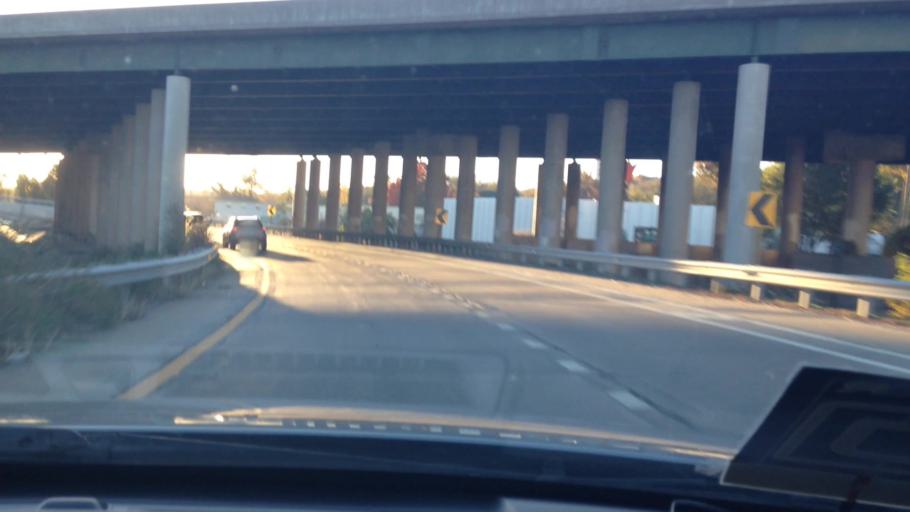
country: US
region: Kansas
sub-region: Johnson County
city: Westwood
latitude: 39.0577
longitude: -94.6279
